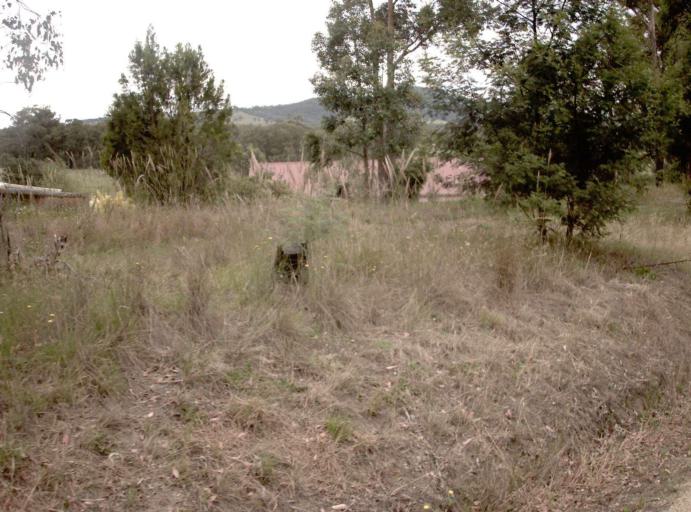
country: AU
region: Victoria
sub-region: East Gippsland
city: Bairnsdale
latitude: -37.7640
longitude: 147.5976
